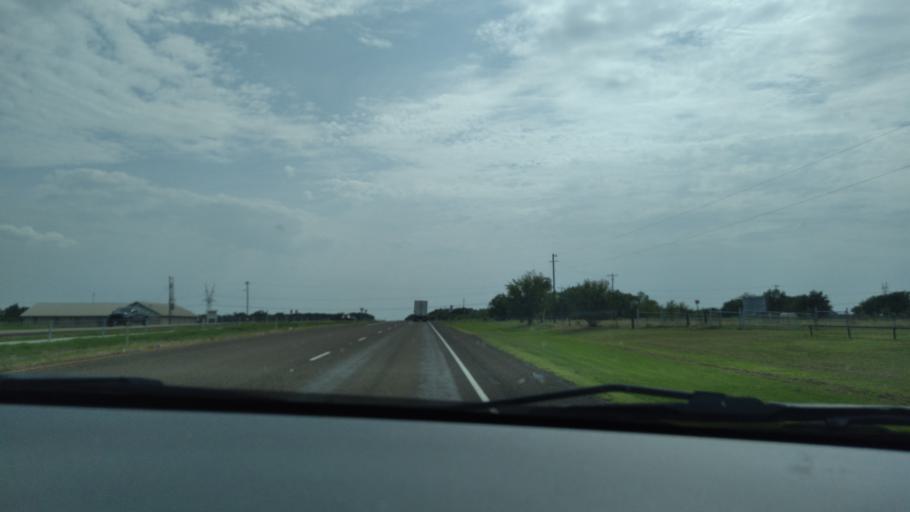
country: US
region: Texas
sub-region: Navarro County
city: Corsicana
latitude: 32.0258
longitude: -96.5690
